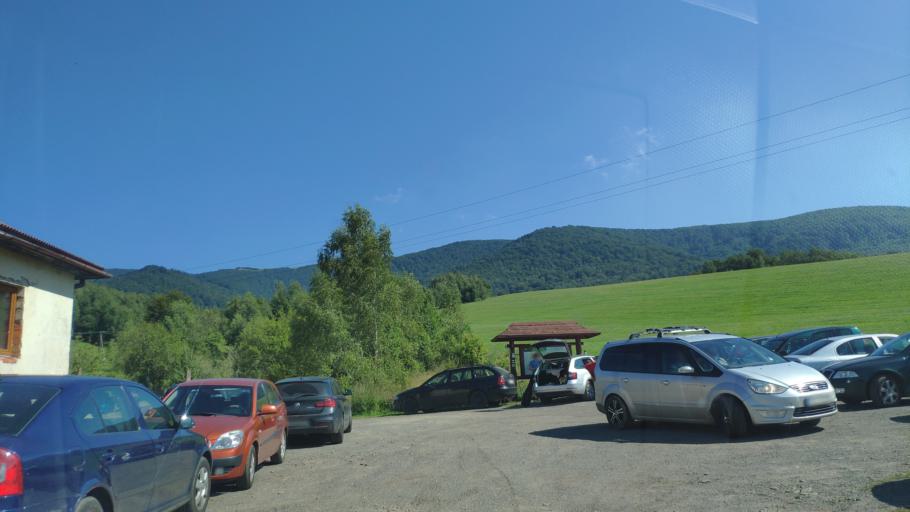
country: PL
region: Subcarpathian Voivodeship
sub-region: Powiat leski
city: Cisna
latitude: 49.0750
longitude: 22.4080
